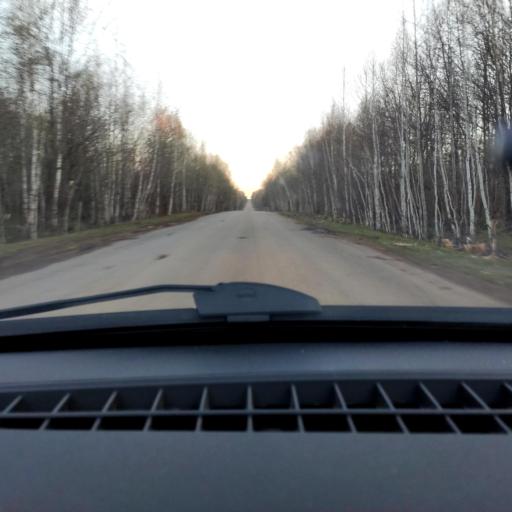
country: RU
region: Bashkortostan
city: Chishmy
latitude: 54.4396
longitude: 55.5596
